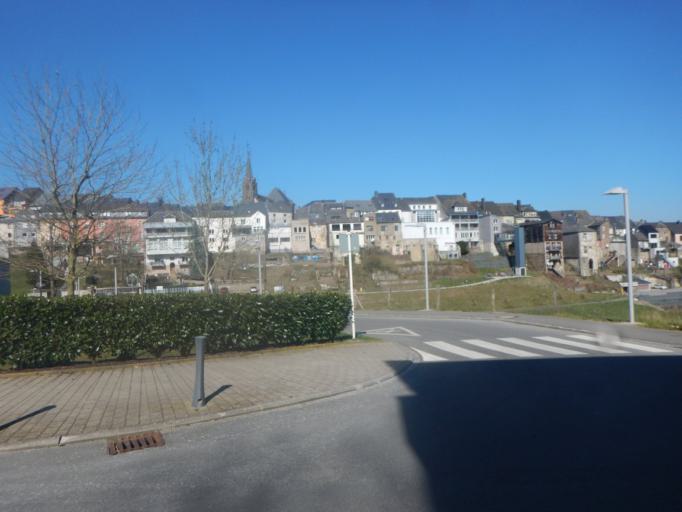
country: LU
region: Diekirch
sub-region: Canton de Wiltz
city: Wiltz
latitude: 49.9636
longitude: 5.9369
